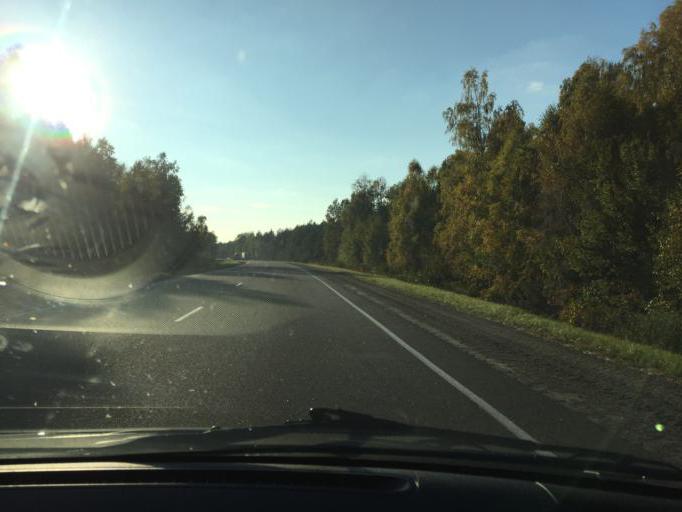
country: BY
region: Brest
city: Asnyezhytsy
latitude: 52.2969
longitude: 26.4352
